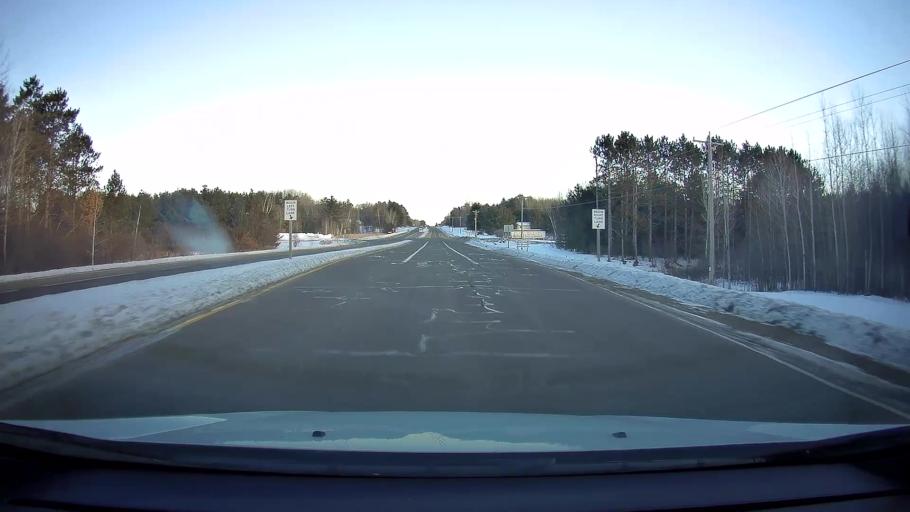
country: US
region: Wisconsin
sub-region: Barron County
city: Cumberland
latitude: 45.5570
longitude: -92.0171
